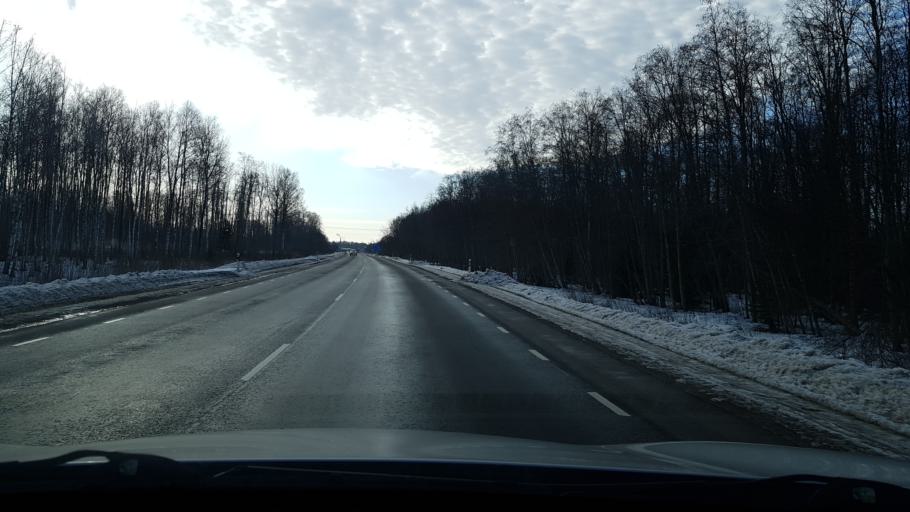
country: EE
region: Viljandimaa
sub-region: Viljandi linn
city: Viljandi
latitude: 58.3826
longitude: 25.5603
